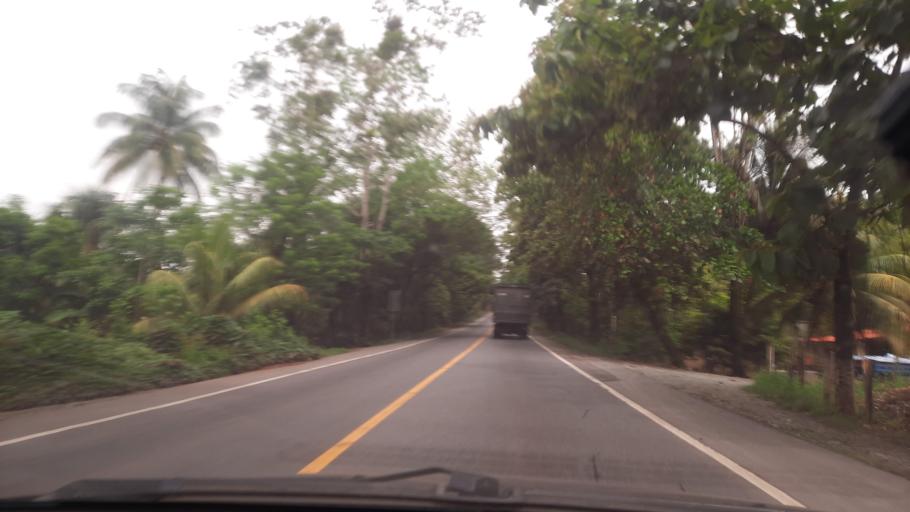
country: GT
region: Izabal
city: Morales
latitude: 15.4631
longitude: -88.9235
